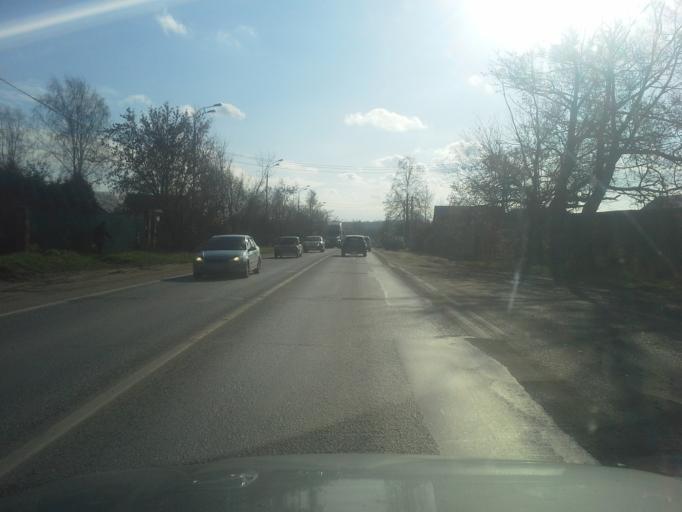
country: RU
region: Moskovskaya
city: Bol'shiye Vyazemy
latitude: 55.6414
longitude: 36.9805
